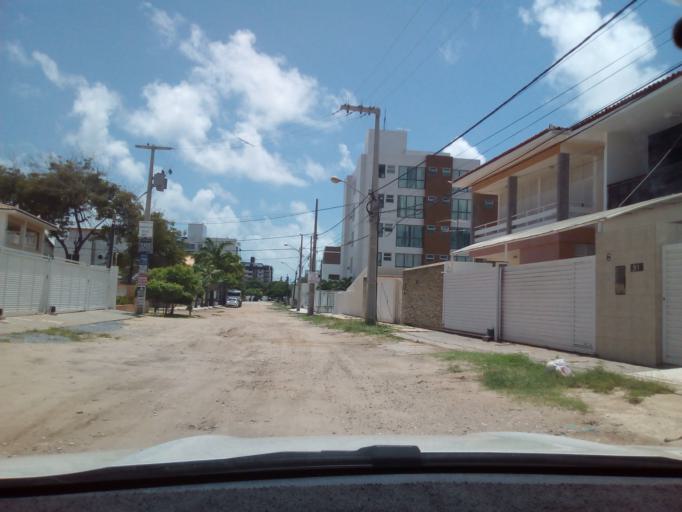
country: BR
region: Paraiba
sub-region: Cabedelo
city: Cabedelo
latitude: -6.9996
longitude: -34.8268
